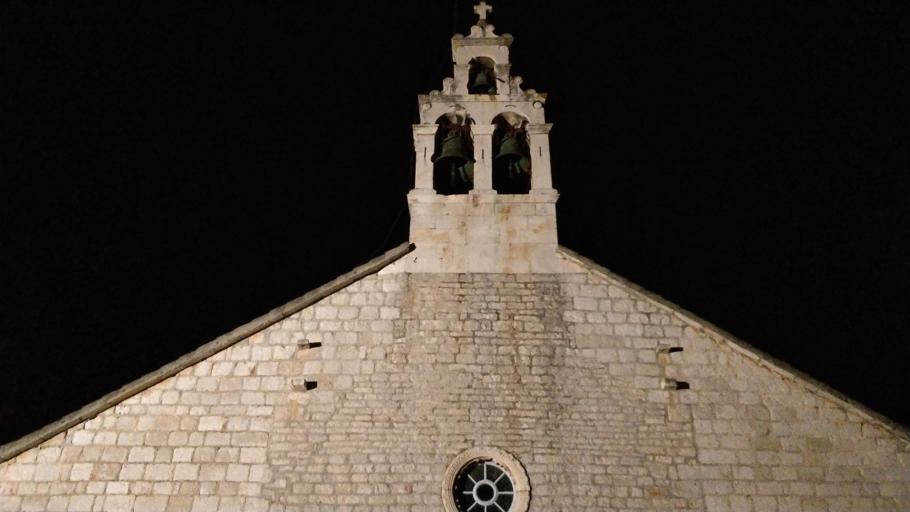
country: HR
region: Splitsko-Dalmatinska
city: Jelsa
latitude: 43.1812
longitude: 16.6699
